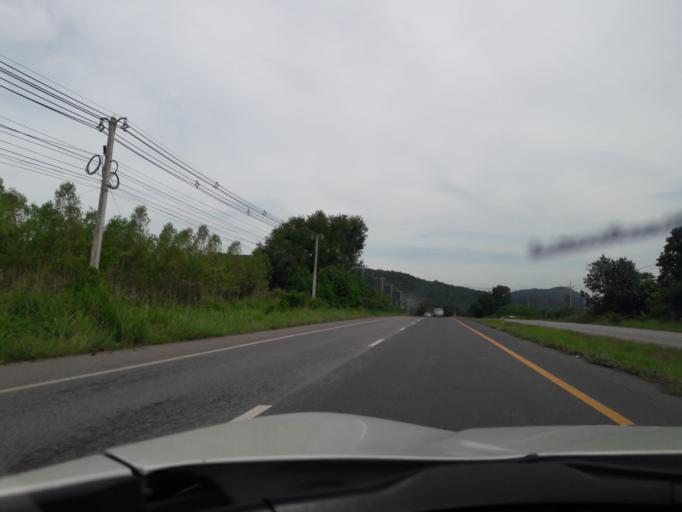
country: TH
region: Lop Buri
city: Chai Badan
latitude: 15.2723
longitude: 101.1243
